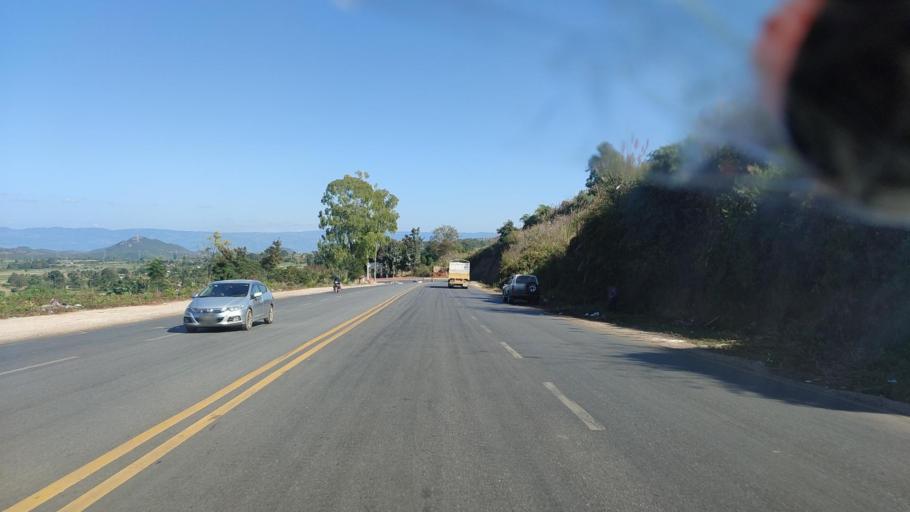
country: MM
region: Mandalay
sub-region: Pyin Oo Lwin District
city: Pyin Oo Lwin
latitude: 22.0775
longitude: 96.5799
